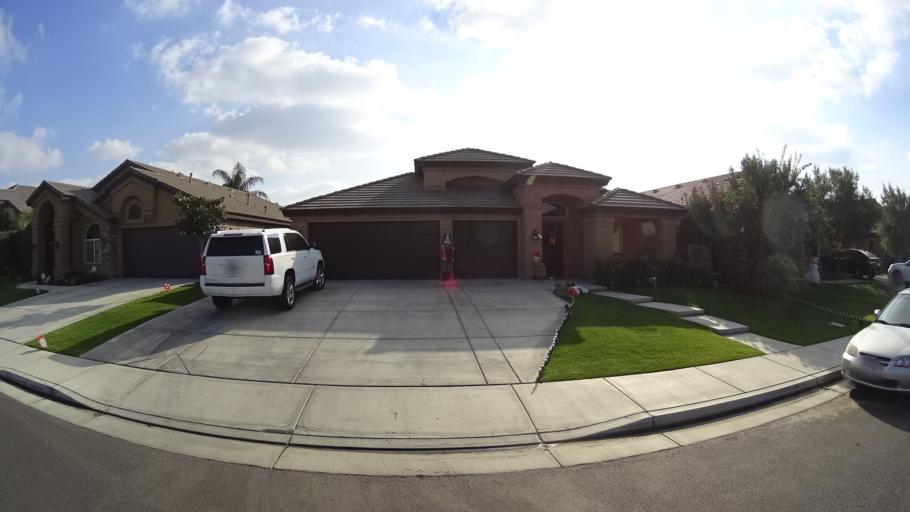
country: US
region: California
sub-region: Kern County
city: Greenacres
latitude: 35.3102
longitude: -119.1071
